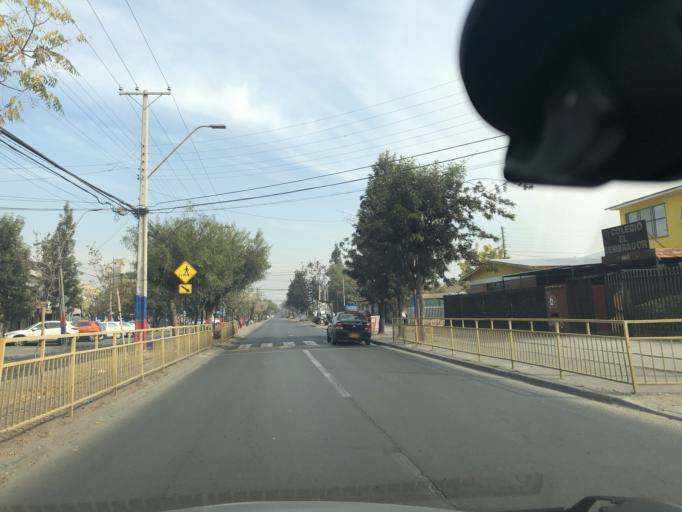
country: CL
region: Santiago Metropolitan
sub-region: Provincia de Cordillera
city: Puente Alto
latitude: -33.5762
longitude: -70.5659
